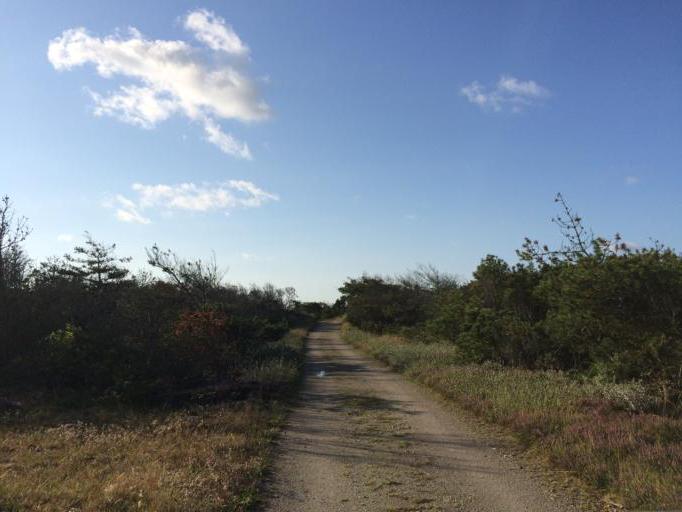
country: DK
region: Central Jutland
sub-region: Holstebro Kommune
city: Ulfborg
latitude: 56.3070
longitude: 8.1352
